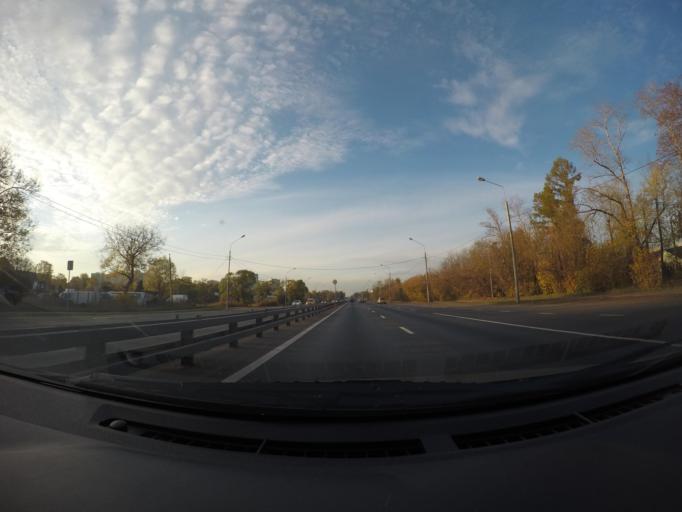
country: RU
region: Moskovskaya
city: Novopodrezkovo
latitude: 55.9430
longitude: 37.3614
